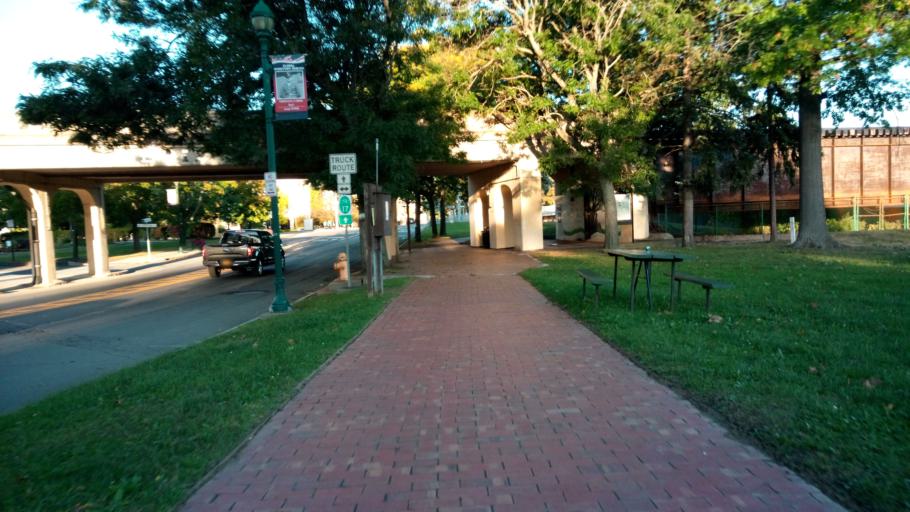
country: US
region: New York
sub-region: Chemung County
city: Elmira
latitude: 42.0878
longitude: -76.8055
